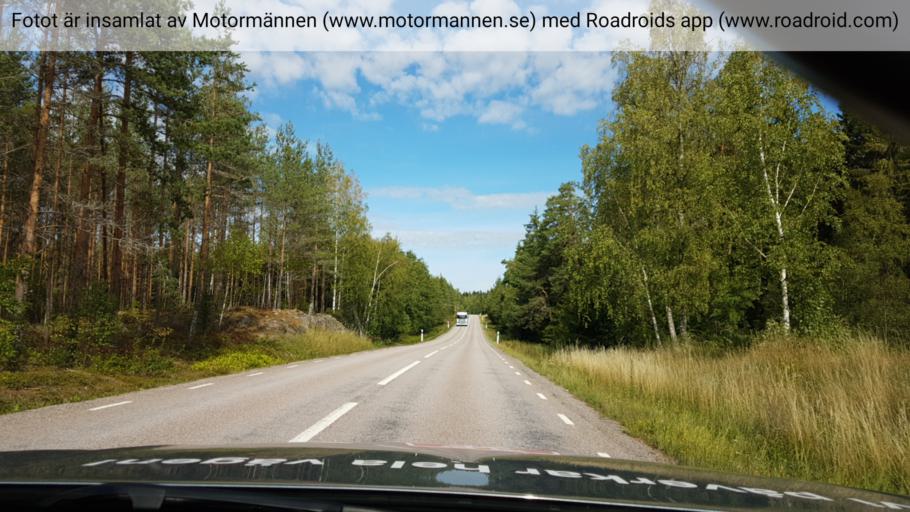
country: SE
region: Uppsala
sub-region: Osthammars Kommun
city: Bjorklinge
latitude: 59.9893
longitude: 17.3236
